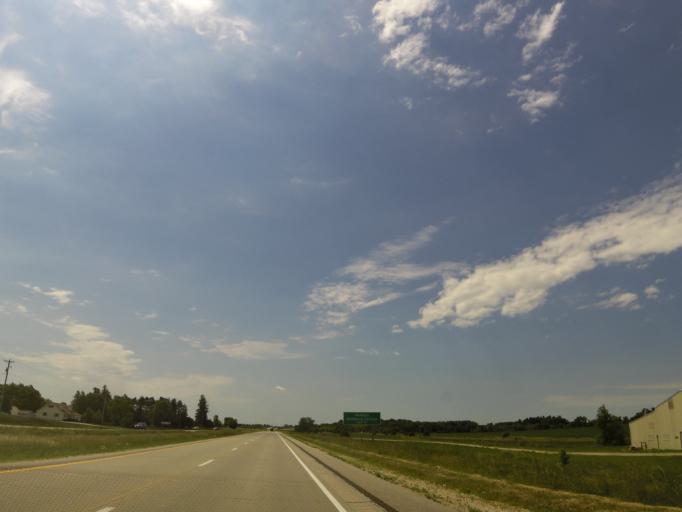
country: US
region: Iowa
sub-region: Bremer County
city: Denver
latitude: 42.7289
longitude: -92.3377
